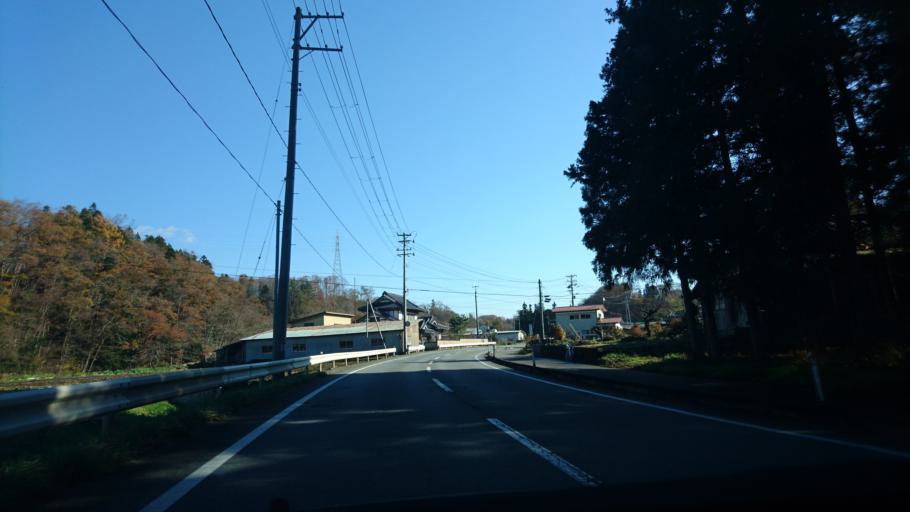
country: JP
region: Iwate
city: Ichinoseki
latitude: 38.9927
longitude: 141.2909
